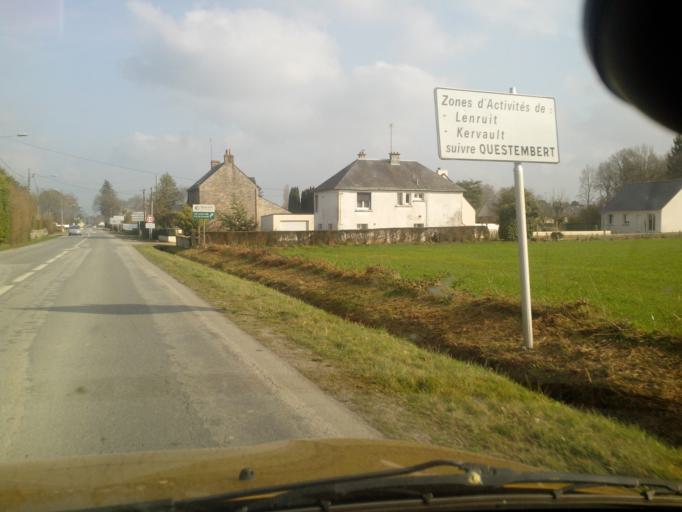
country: FR
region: Brittany
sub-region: Departement du Morbihan
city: Questembert
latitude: 47.6861
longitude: -2.4553
